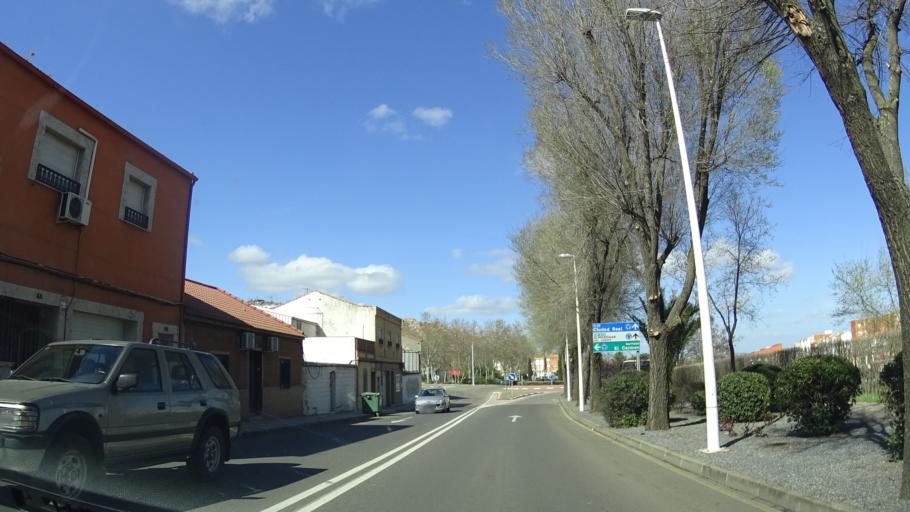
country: ES
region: Castille-La Mancha
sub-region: Provincia de Ciudad Real
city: Puertollano
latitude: 38.6880
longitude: -4.1135
